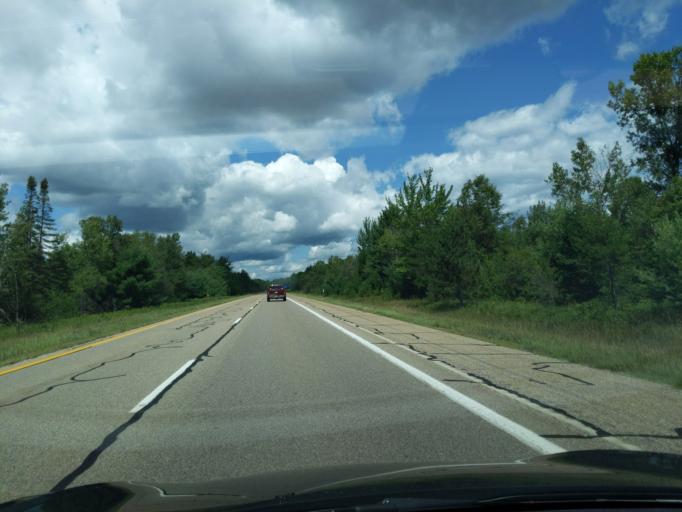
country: US
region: Michigan
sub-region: Roscommon County
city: Houghton Lake
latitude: 44.3034
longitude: -84.8023
